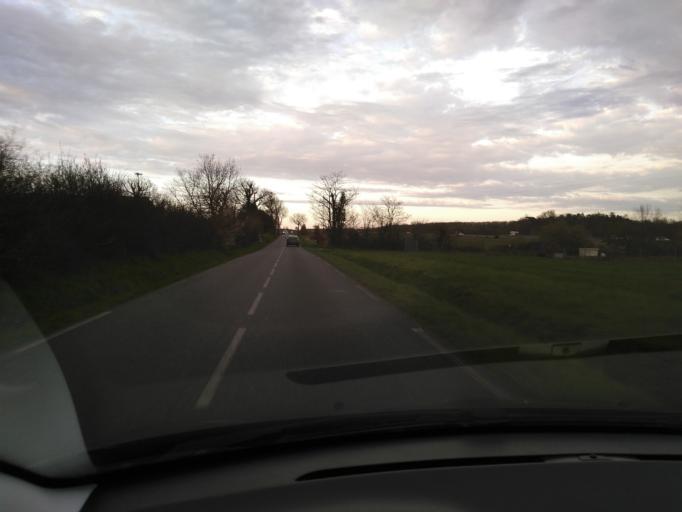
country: FR
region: Midi-Pyrenees
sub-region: Departement de la Haute-Garonne
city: La Salvetat-Saint-Gilles
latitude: 43.5922
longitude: 1.2739
